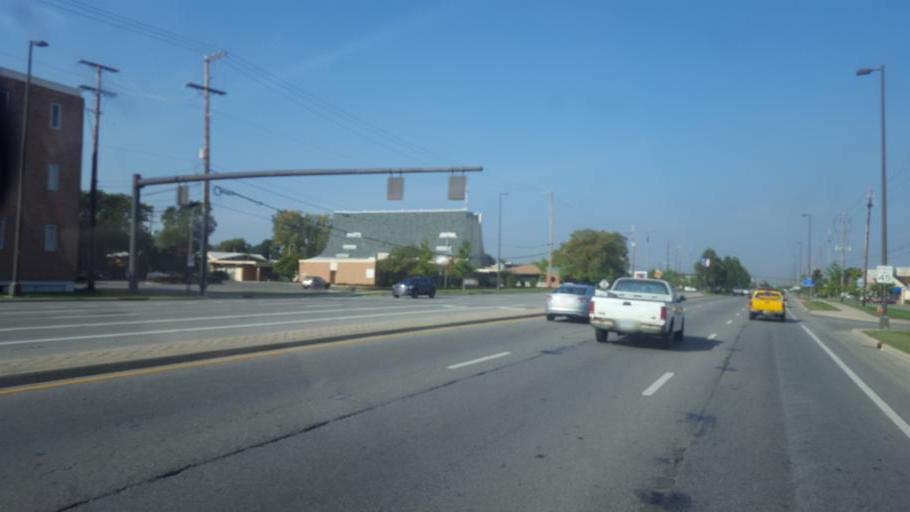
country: US
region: Ohio
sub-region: Franklin County
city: Minerva Park
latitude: 40.0608
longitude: -82.9791
